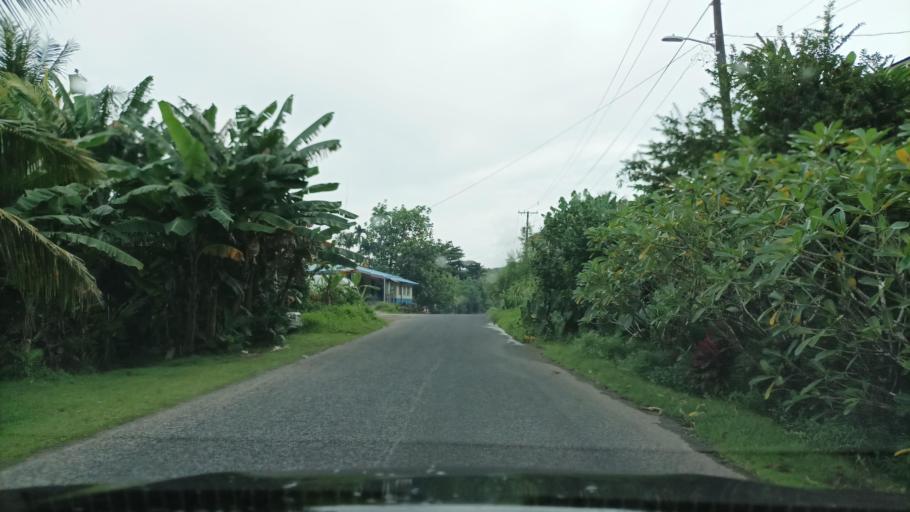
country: FM
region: Pohnpei
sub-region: Kolonia Municipality
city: Kolonia
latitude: 6.9541
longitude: 158.2776
